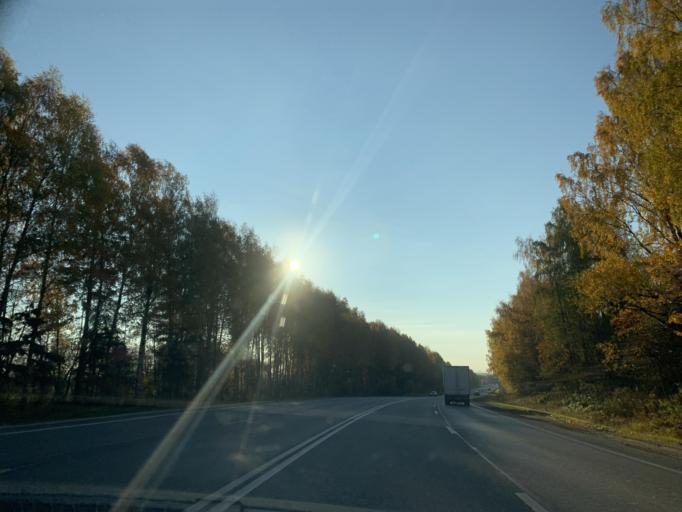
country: RU
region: Jaroslavl
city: Konstantinovskiy
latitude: 57.7738
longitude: 39.6649
